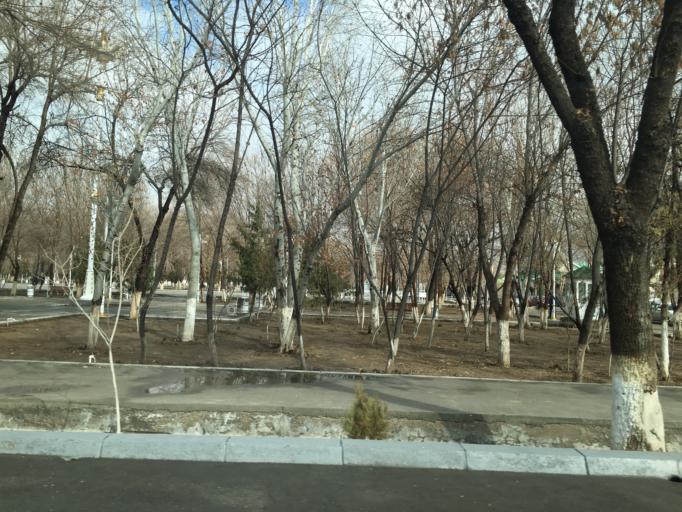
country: TM
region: Ahal
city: Ashgabat
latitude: 37.9455
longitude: 58.3623
